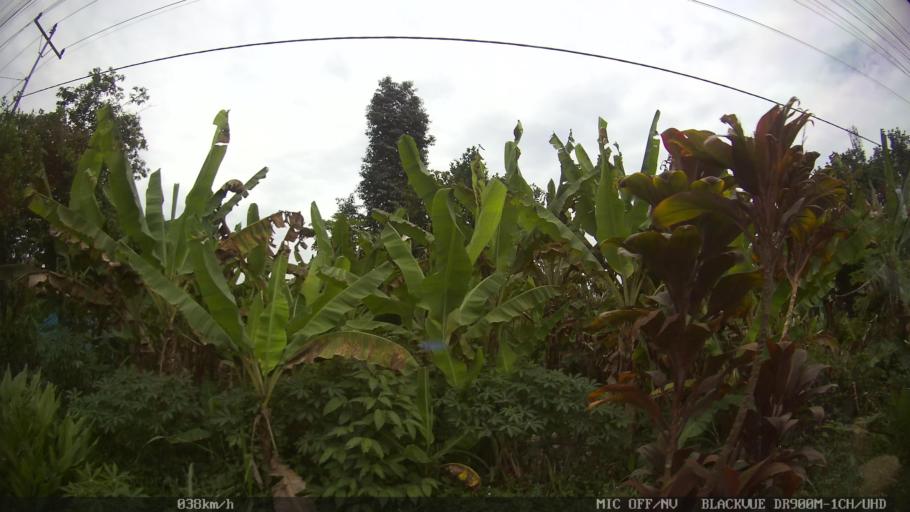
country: ID
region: North Sumatra
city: Sunggal
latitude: 3.6314
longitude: 98.5633
